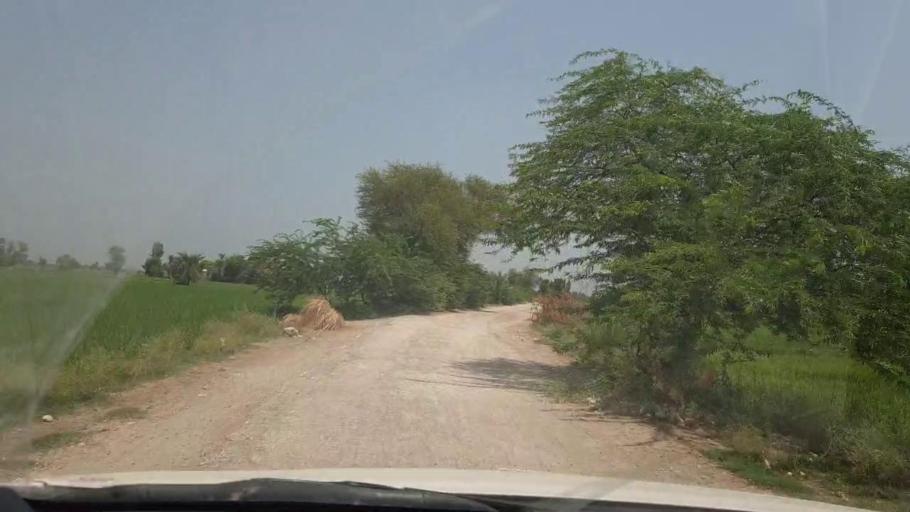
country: PK
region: Sindh
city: Shikarpur
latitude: 27.9182
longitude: 68.6884
